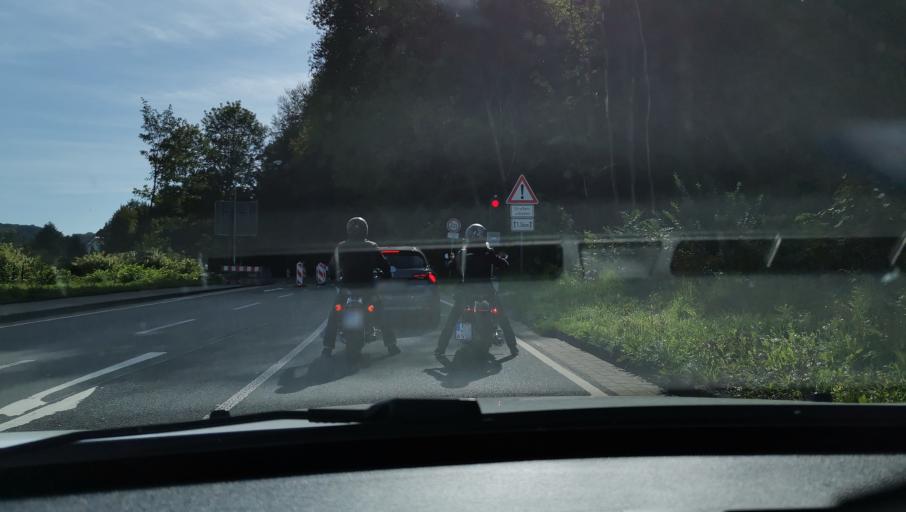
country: DE
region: North Rhine-Westphalia
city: Kierspe
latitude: 51.1225
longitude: 7.6042
